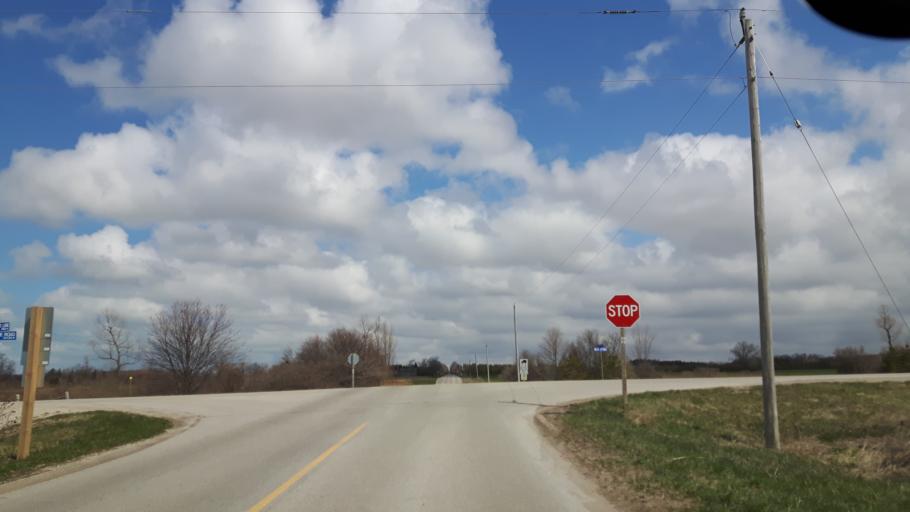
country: CA
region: Ontario
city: Goderich
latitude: 43.6425
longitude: -81.6846
